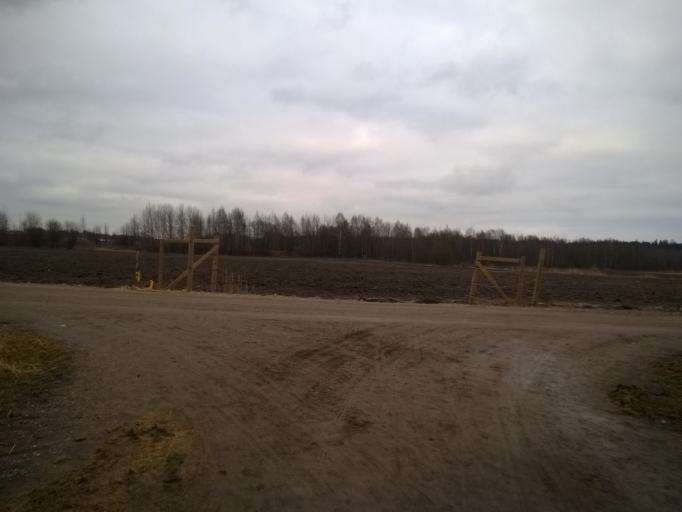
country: FI
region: Uusimaa
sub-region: Helsinki
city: Vantaa
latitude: 60.2210
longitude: 25.0253
